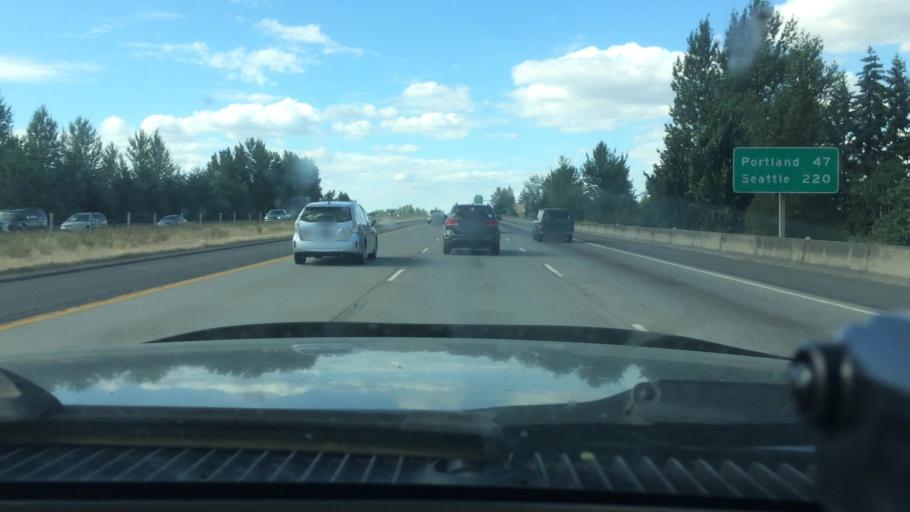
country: US
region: Oregon
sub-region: Marion County
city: Four Corners
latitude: 44.9252
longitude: -122.9902
